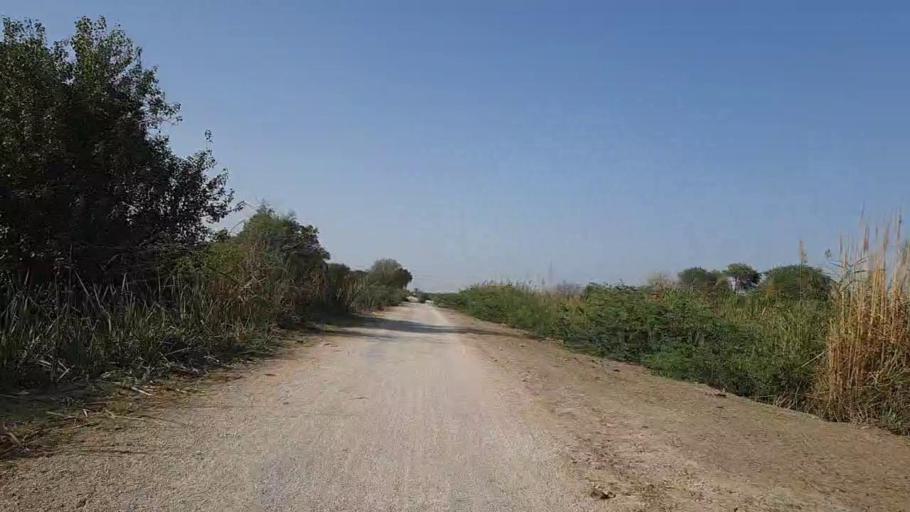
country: PK
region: Sindh
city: Kotri
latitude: 25.1462
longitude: 68.2655
